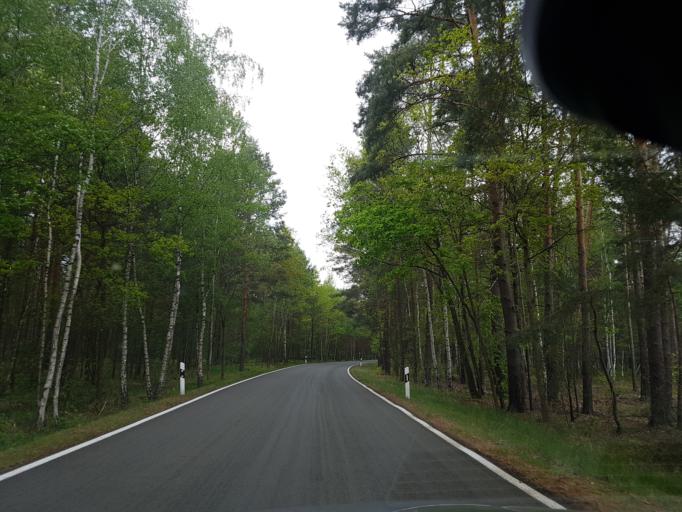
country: DE
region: Brandenburg
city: Crinitz
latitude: 51.7503
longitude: 13.7530
